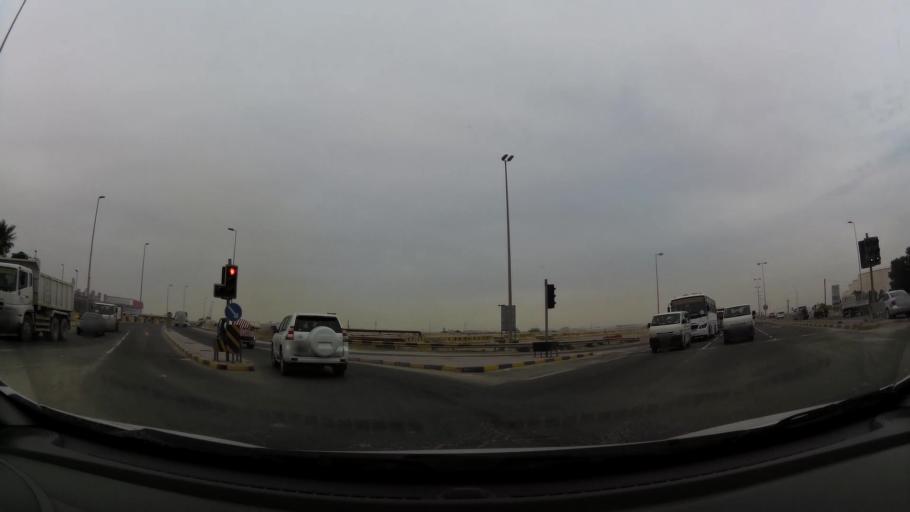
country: BH
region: Northern
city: Sitrah
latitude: 26.0982
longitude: 50.6060
